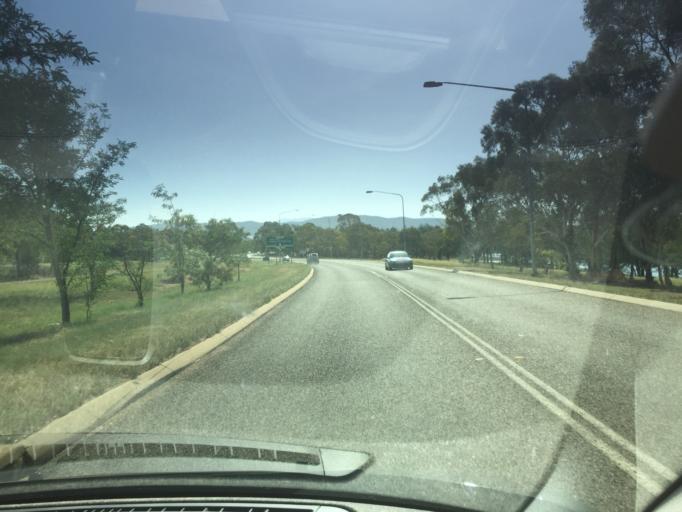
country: AU
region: Australian Capital Territory
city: Macarthur
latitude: -35.4229
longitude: 149.0825
